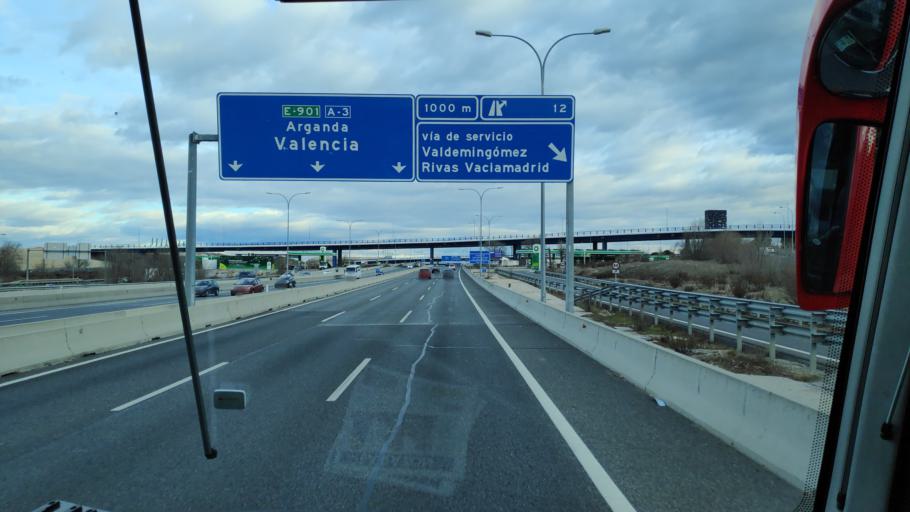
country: ES
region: Madrid
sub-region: Provincia de Madrid
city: Villa de Vallecas
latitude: 40.3722
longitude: -3.5946
